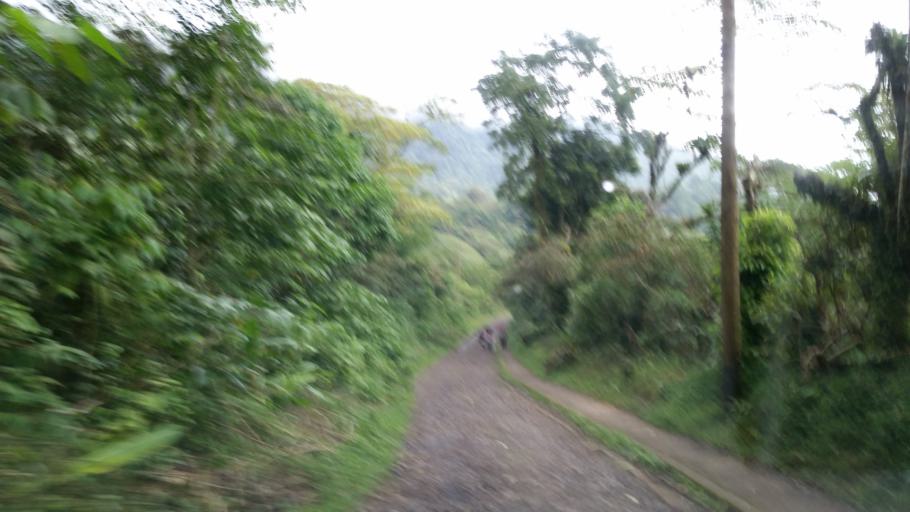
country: NI
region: Jinotega
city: San Jose de Bocay
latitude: 13.2776
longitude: -85.7174
